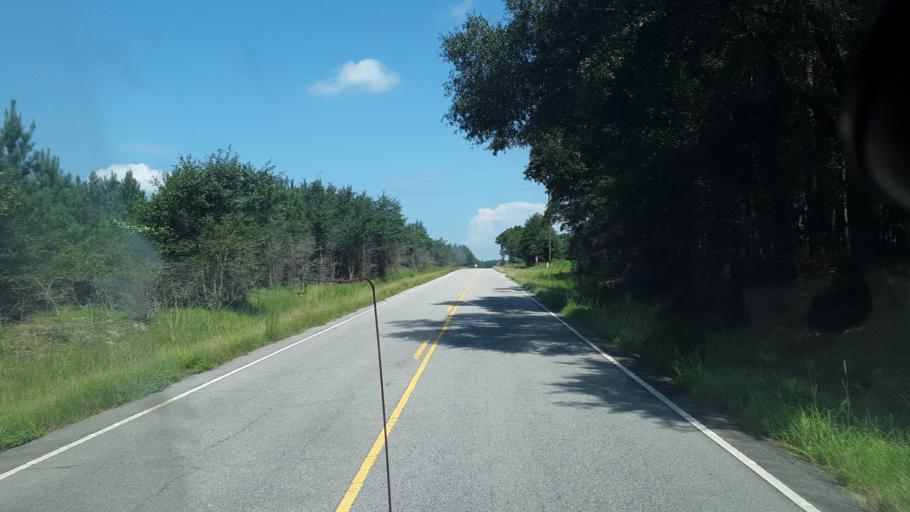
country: US
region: South Carolina
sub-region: Bamberg County
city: Bamberg
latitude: 33.4050
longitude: -81.0160
